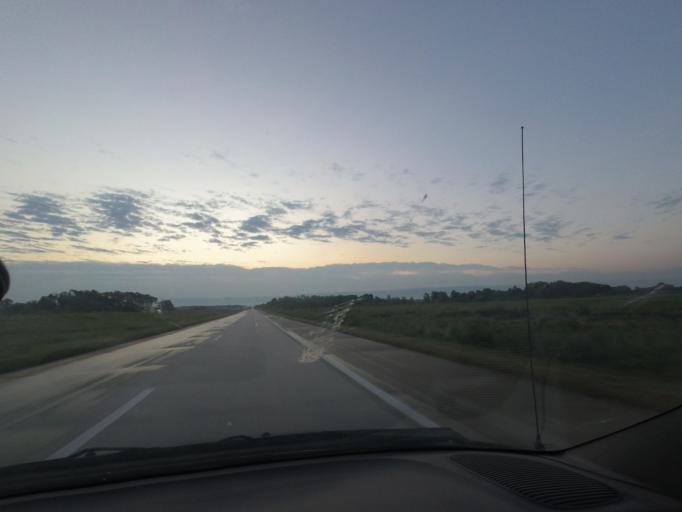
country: US
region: Missouri
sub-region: Macon County
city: Macon
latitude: 39.7603
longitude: -92.6958
